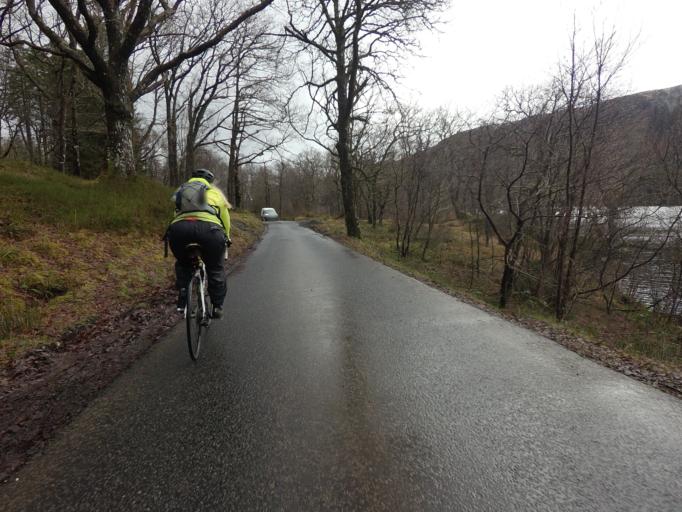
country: GB
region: Scotland
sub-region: West Dunbartonshire
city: Balloch
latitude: 56.2210
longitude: -4.5498
